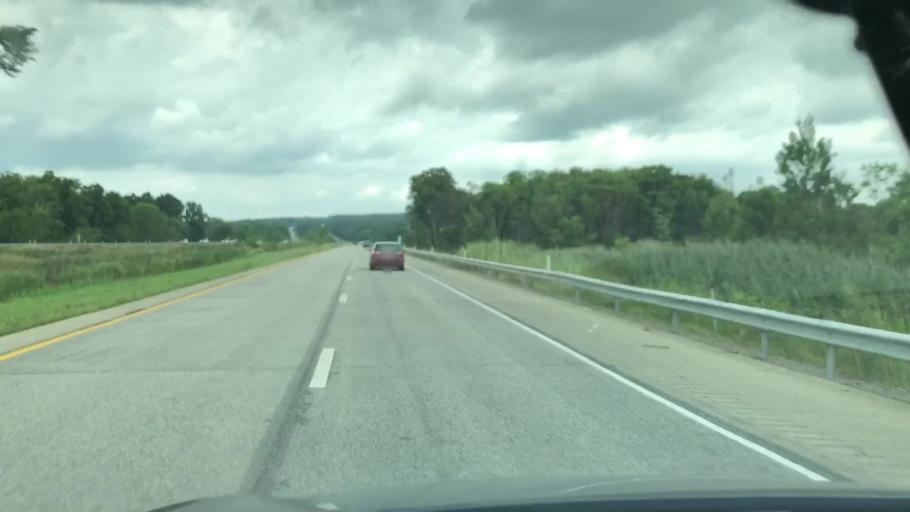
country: US
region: Pennsylvania
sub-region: Erie County
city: Edinboro
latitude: 41.8977
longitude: -80.1753
